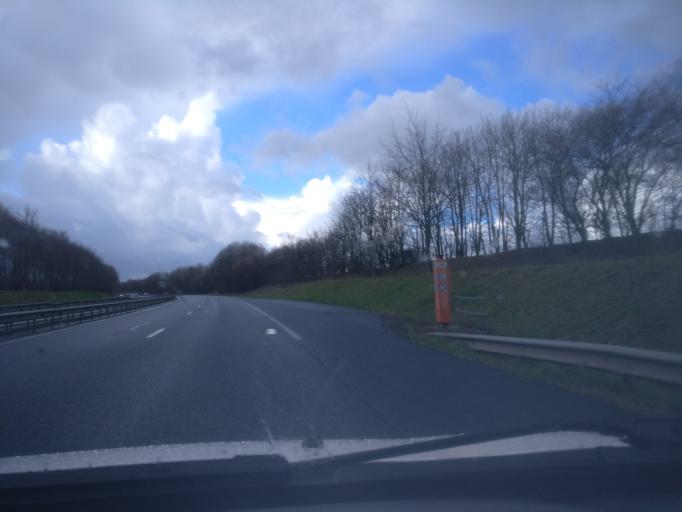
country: FR
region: Lower Normandy
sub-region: Departement du Calvados
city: Grainville-sur-Odon
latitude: 49.1436
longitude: -0.5319
